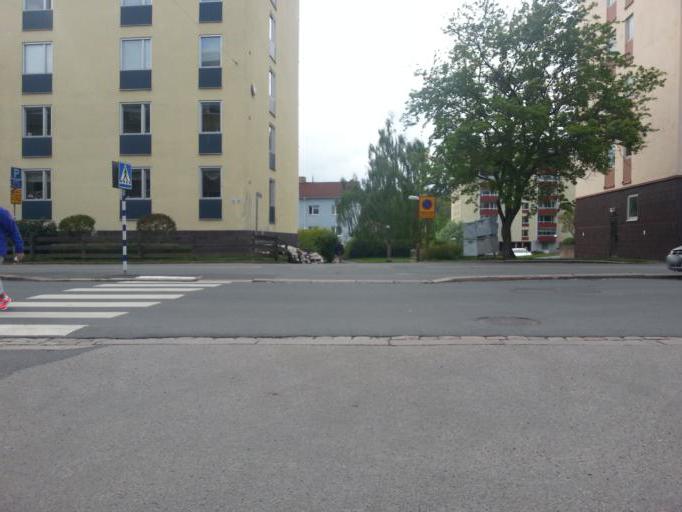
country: SE
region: Joenkoeping
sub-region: Jonkopings Kommun
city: Jonkoping
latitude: 57.7779
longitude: 14.1540
